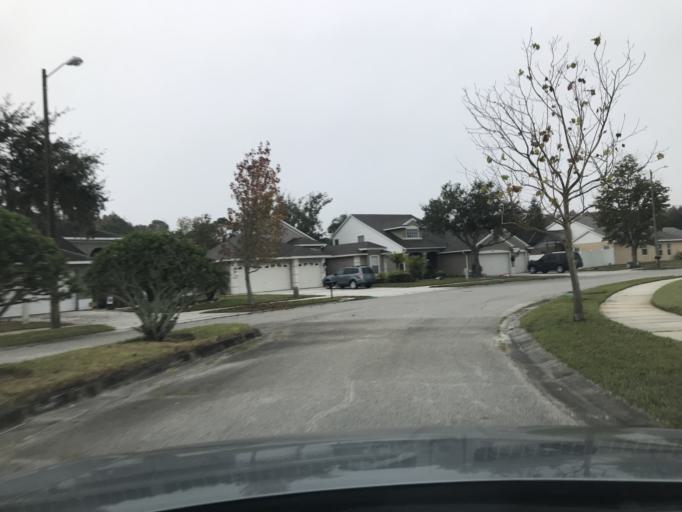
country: US
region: Florida
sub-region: Pinellas County
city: Oldsmar
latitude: 28.0509
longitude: -82.6636
